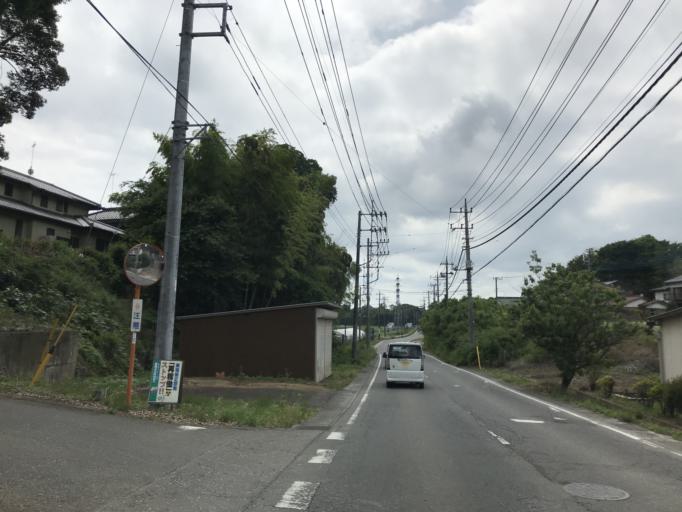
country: JP
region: Ibaraki
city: Ushiku
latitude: 35.9760
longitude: 140.0948
